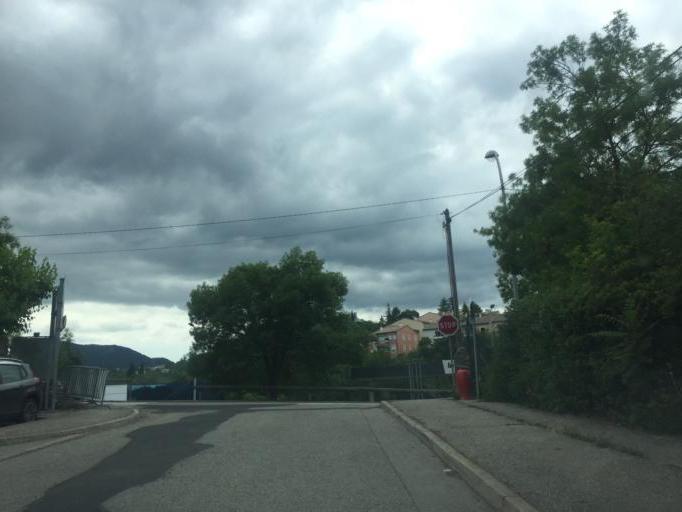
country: FR
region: Rhone-Alpes
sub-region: Departement de l'Ardeche
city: Privas
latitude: 44.7265
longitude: 4.5973
